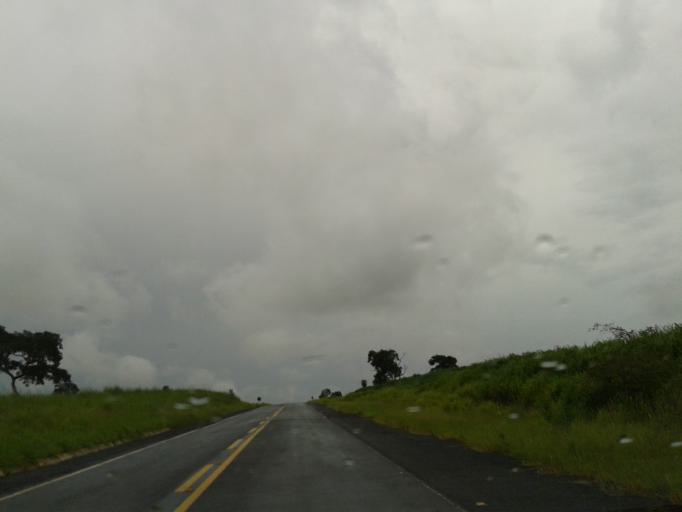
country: BR
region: Minas Gerais
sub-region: Santa Vitoria
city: Santa Vitoria
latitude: -19.1563
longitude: -50.1259
